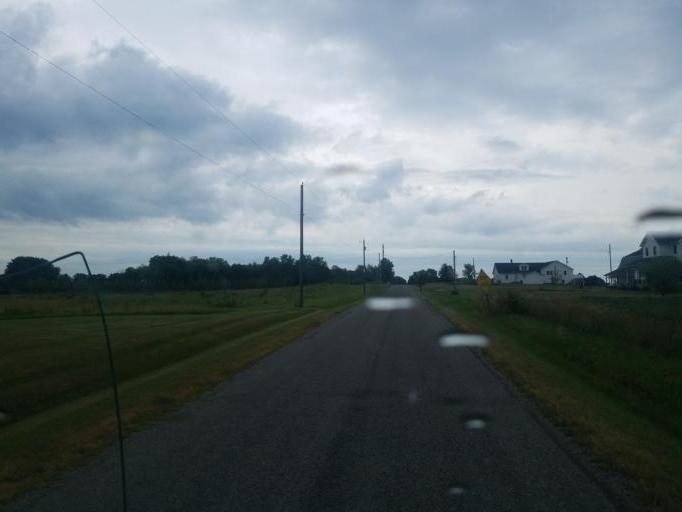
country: US
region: Ohio
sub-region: Defiance County
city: Hicksville
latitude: 41.3681
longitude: -84.7693
